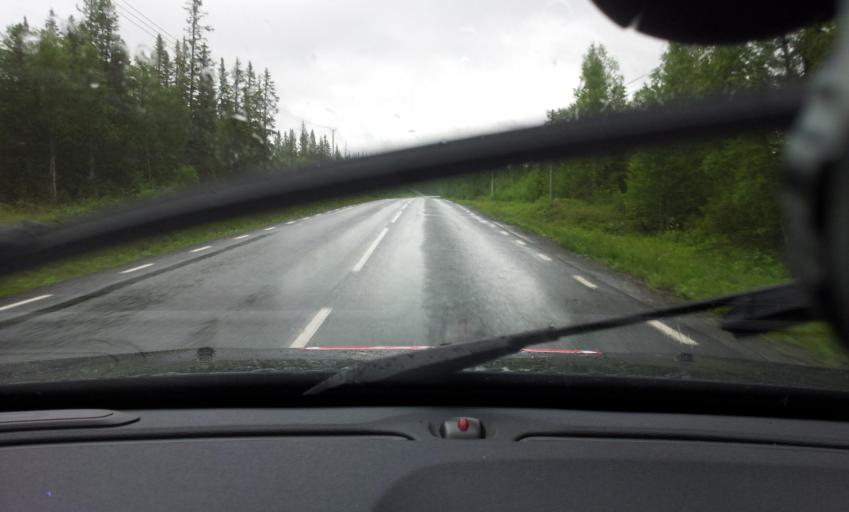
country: SE
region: Jaemtland
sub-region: Are Kommun
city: Are
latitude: 63.2398
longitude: 13.1766
